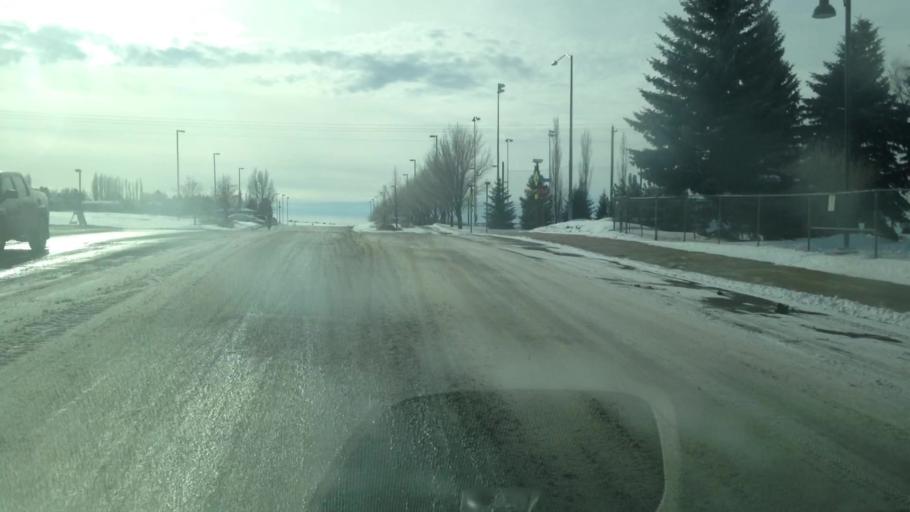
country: US
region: Idaho
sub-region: Madison County
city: Rexburg
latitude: 43.8122
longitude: -111.7838
